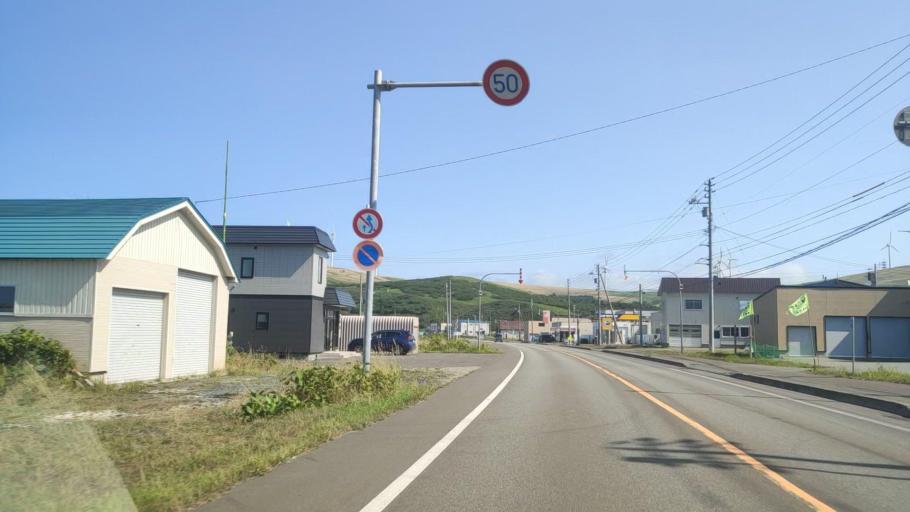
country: JP
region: Hokkaido
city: Makubetsu
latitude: 45.4598
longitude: 141.8785
